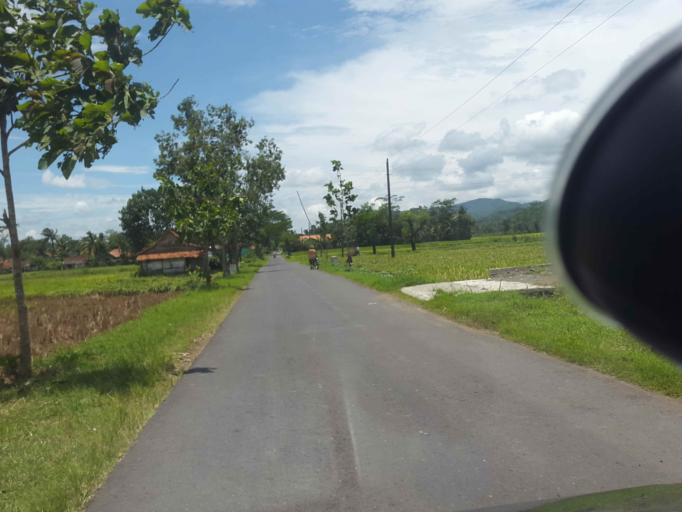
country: ID
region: Central Java
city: Gerduren
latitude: -7.4895
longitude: 109.1129
